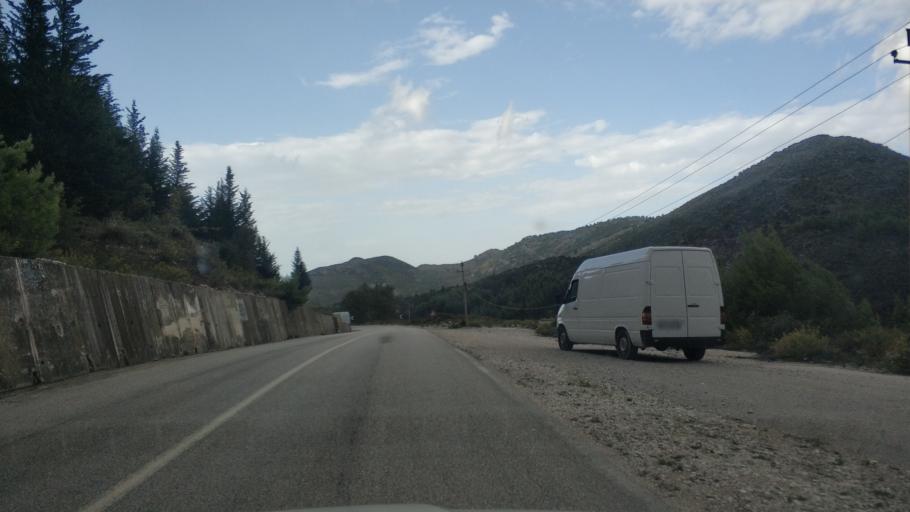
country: AL
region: Vlore
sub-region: Rrethi i Vlores
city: Orikum
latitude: 40.2604
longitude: 19.5243
